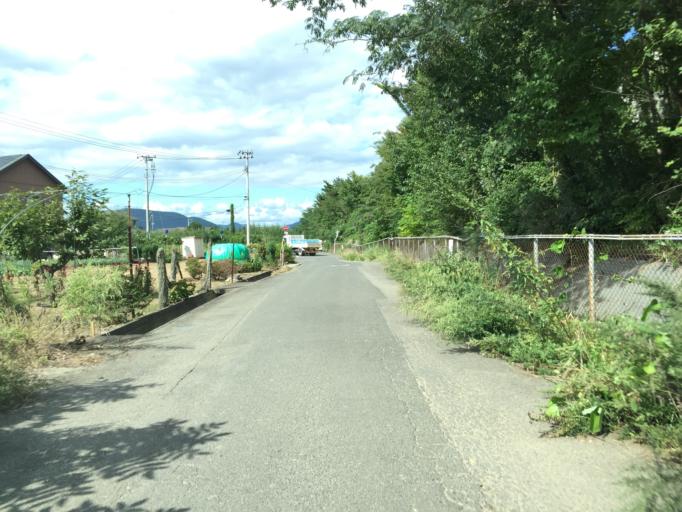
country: JP
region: Fukushima
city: Fukushima-shi
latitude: 37.7722
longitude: 140.4126
